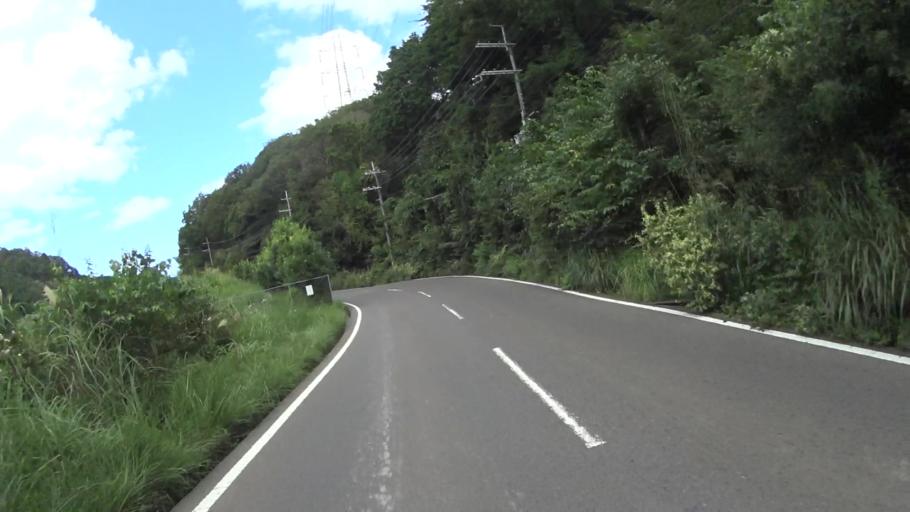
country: JP
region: Shiga Prefecture
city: Otsu-shi
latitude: 34.9236
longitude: 135.8857
